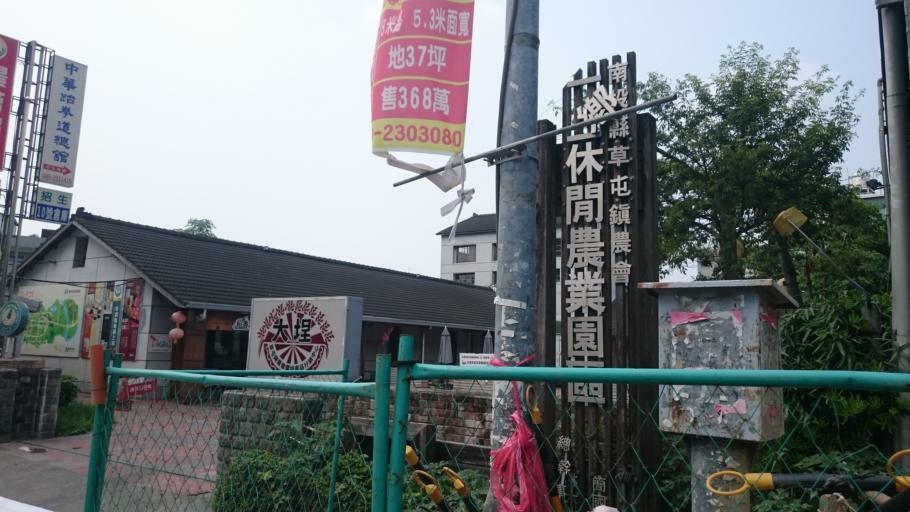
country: TW
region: Taiwan
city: Zhongxing New Village
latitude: 23.9781
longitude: 120.6823
